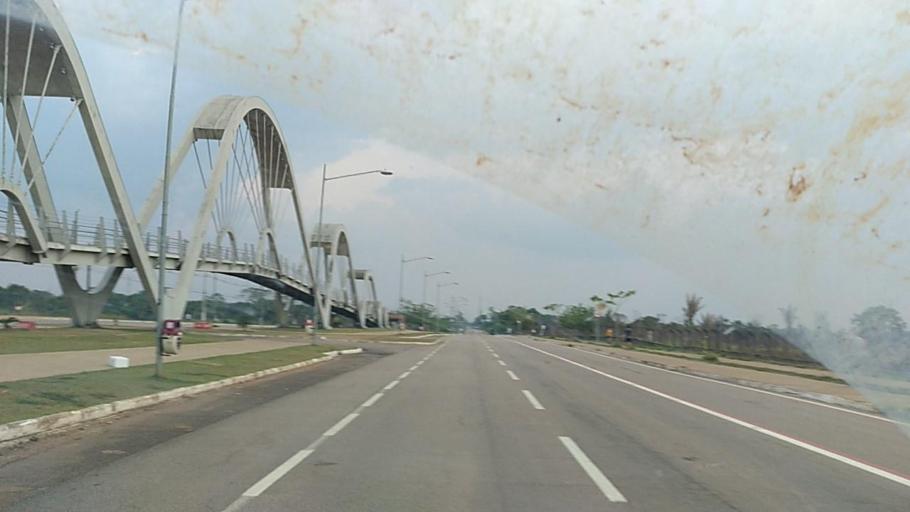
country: BR
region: Rondonia
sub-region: Porto Velho
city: Porto Velho
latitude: -8.7263
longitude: -63.8933
